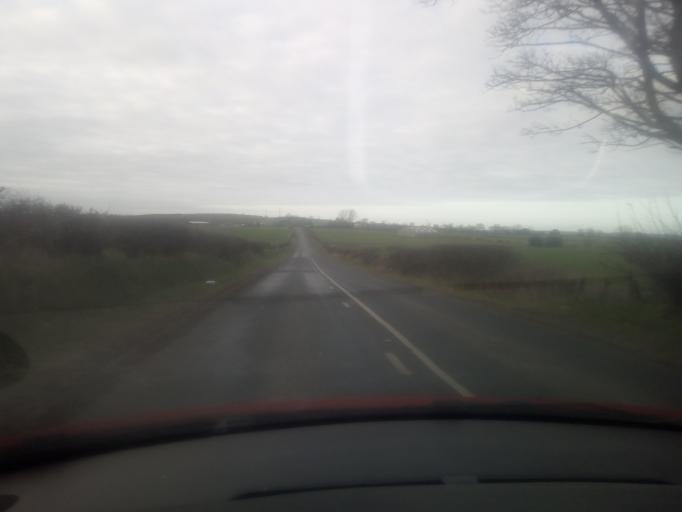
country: GB
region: England
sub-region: Darlington
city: Summerhouse
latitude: 54.6016
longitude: -1.6806
